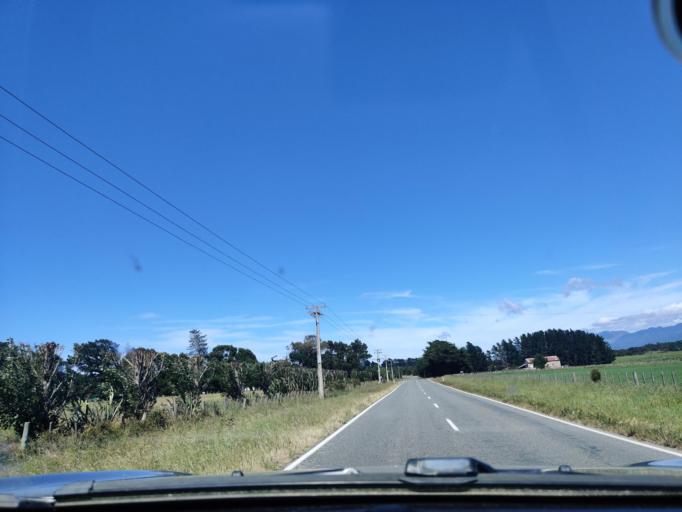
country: NZ
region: Wellington
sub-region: Upper Hutt City
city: Upper Hutt
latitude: -41.3192
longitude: 175.2549
